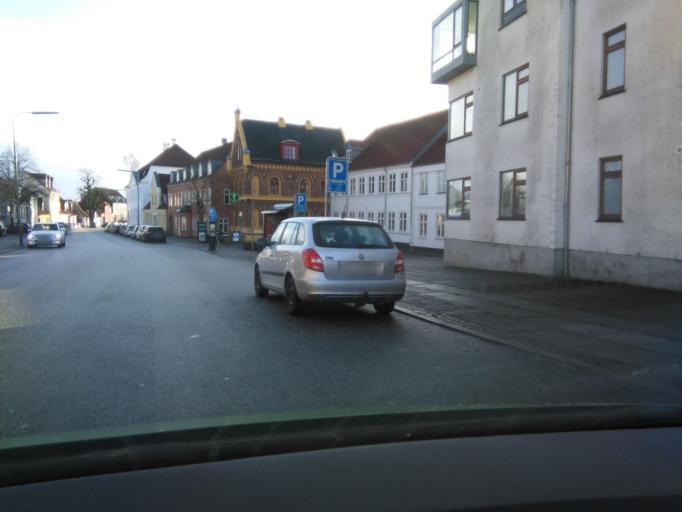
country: DK
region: Central Jutland
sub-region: Skanderborg Kommune
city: Skanderborg
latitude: 56.0312
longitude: 9.9330
